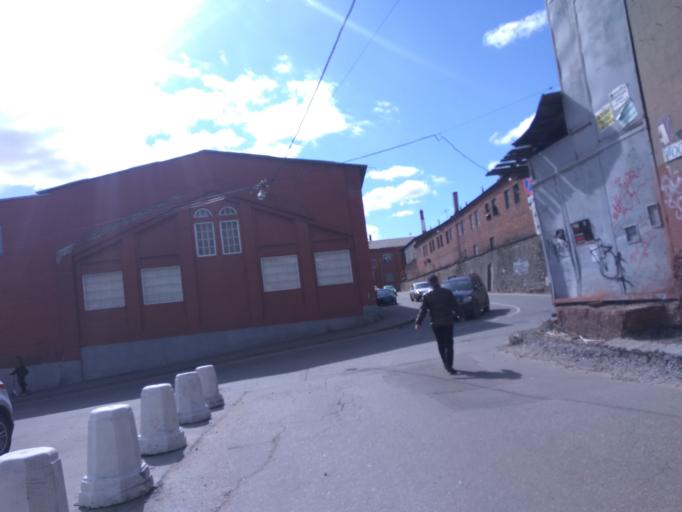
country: RU
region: Moscow
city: Taganskiy
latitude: 55.7571
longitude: 37.6645
